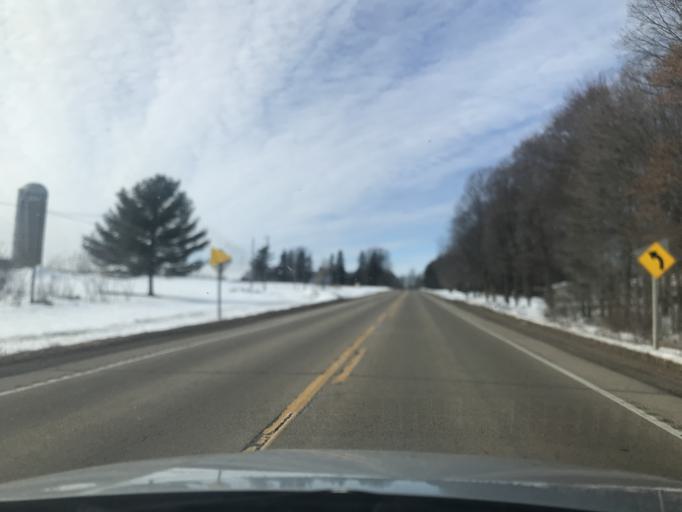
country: US
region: Wisconsin
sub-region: Oconto County
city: Gillett
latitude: 44.8861
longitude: -88.3249
